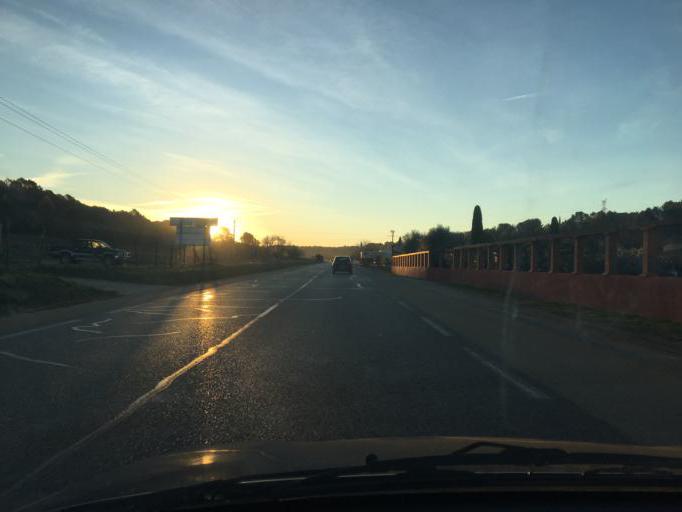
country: FR
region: Provence-Alpes-Cote d'Azur
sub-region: Departement du Var
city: Lorgues
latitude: 43.4726
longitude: 6.3788
